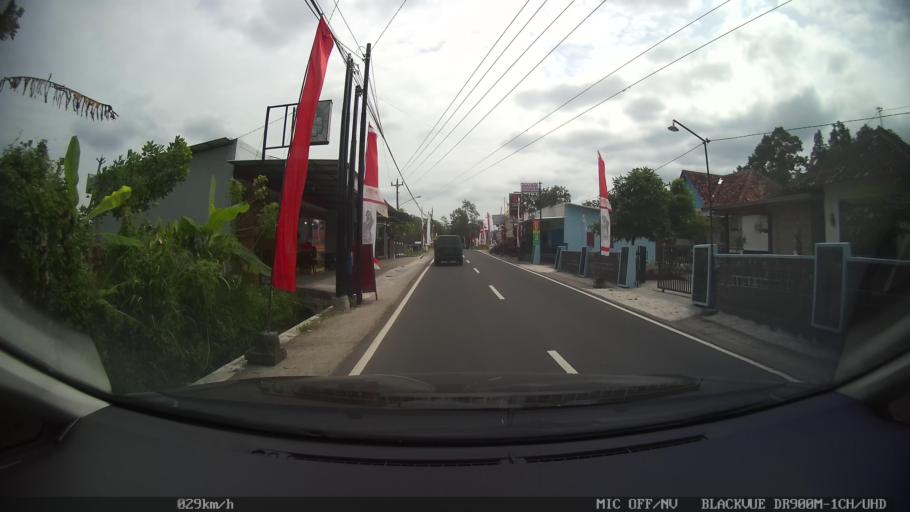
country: ID
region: Central Java
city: Candi Prambanan
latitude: -7.7317
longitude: 110.4596
